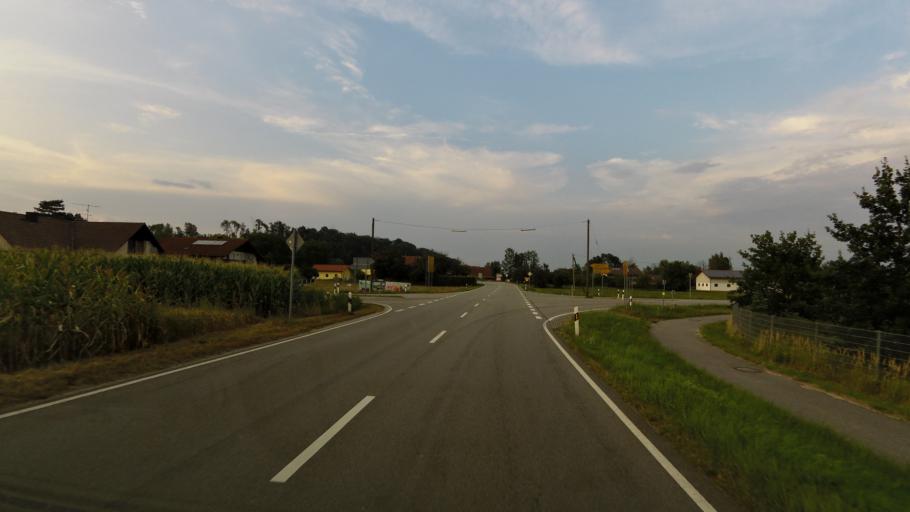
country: DE
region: Bavaria
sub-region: Lower Bavaria
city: Kirchham
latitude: 48.3478
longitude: 13.2473
